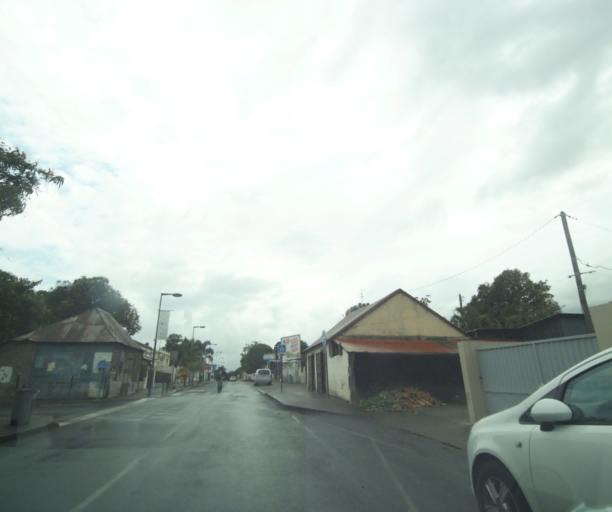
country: RE
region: Reunion
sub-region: Reunion
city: Saint-Paul
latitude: -21.0067
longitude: 55.2763
